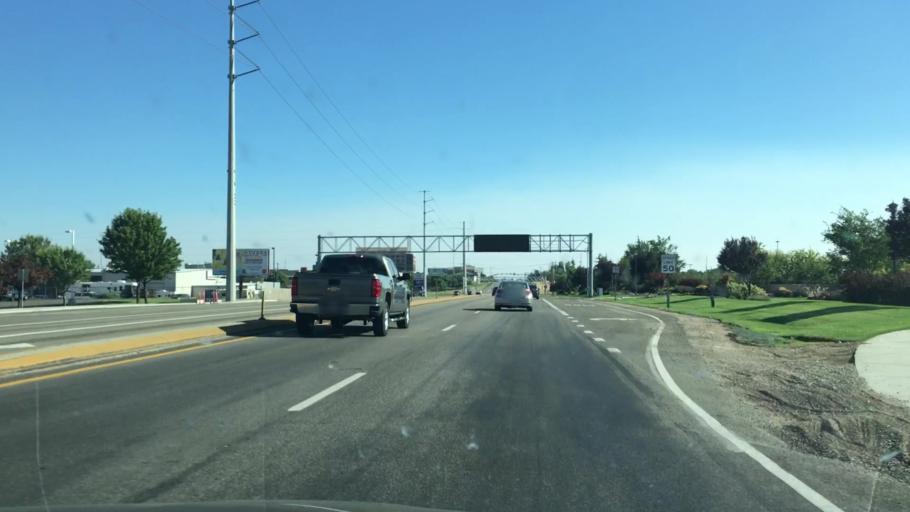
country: US
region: Idaho
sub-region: Ada County
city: Meridian
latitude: 43.6120
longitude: -116.3548
